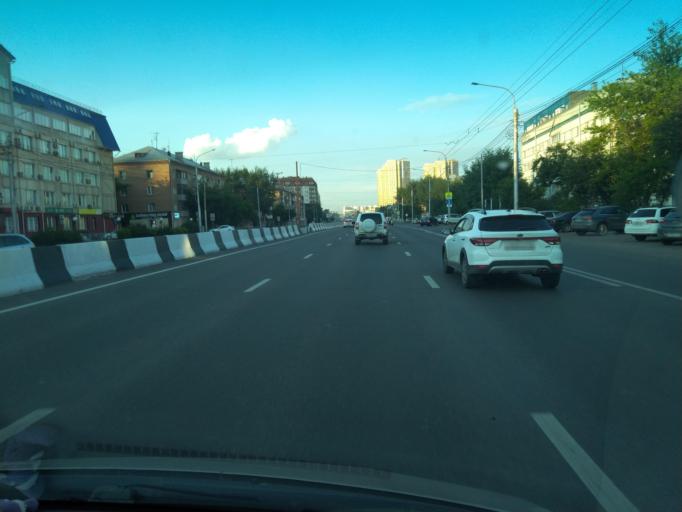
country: RU
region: Krasnoyarskiy
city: Krasnoyarsk
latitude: 56.0287
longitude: 92.9132
